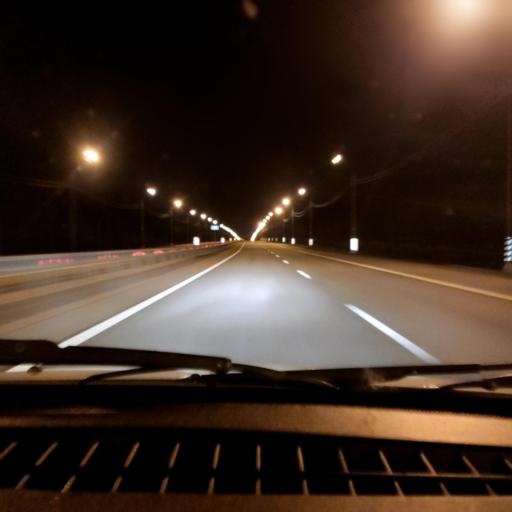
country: RU
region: Lipetsk
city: Zadonsk
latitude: 52.3310
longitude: 39.0103
